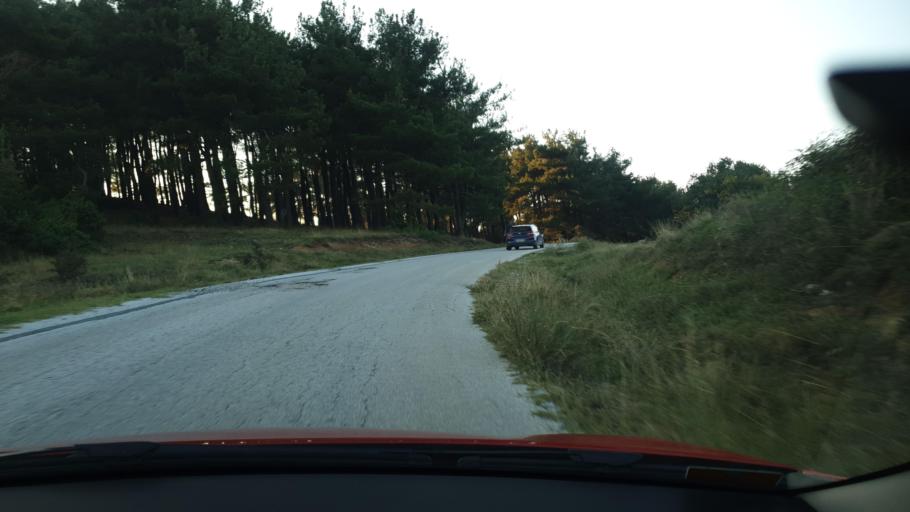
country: GR
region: Central Macedonia
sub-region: Nomos Thessalonikis
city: Peristera
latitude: 40.5104
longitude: 23.2198
